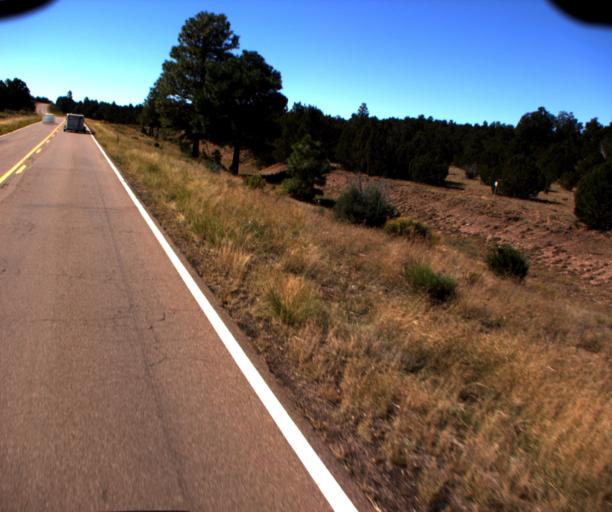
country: US
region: Arizona
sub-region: Navajo County
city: Heber-Overgaard
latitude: 34.4466
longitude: -110.5294
